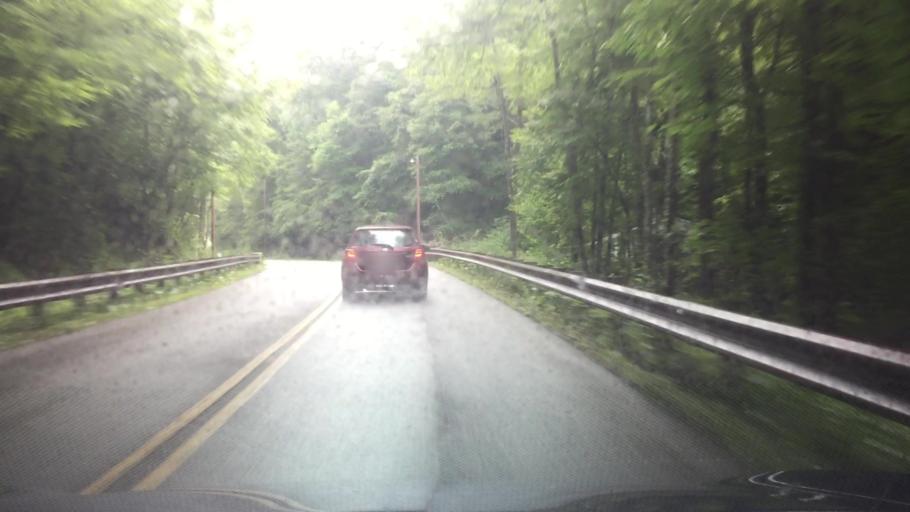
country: US
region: Virginia
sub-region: Smyth County
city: Atkins
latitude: 36.8291
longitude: -81.4157
